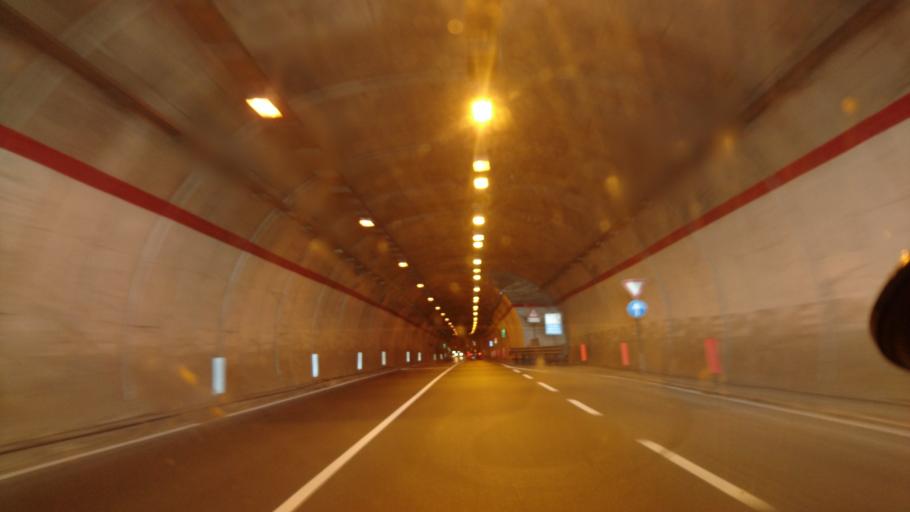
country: IT
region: Liguria
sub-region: Provincia di Savona
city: Bergeggi
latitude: 44.2550
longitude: 8.4509
